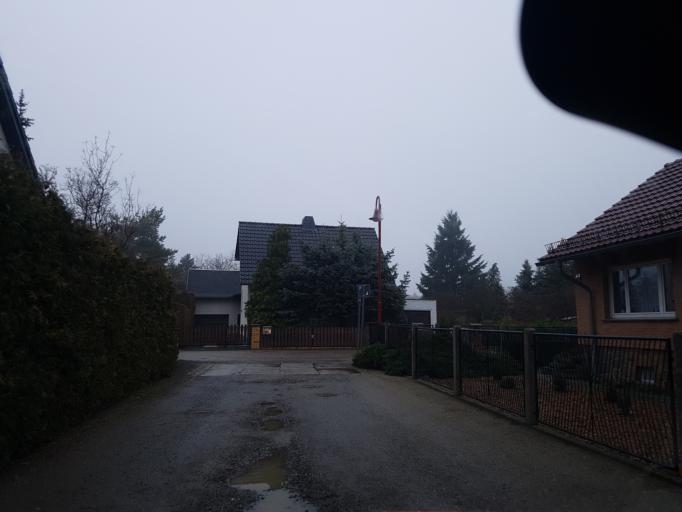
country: DE
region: Brandenburg
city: Finsterwalde
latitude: 51.6489
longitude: 13.7009
